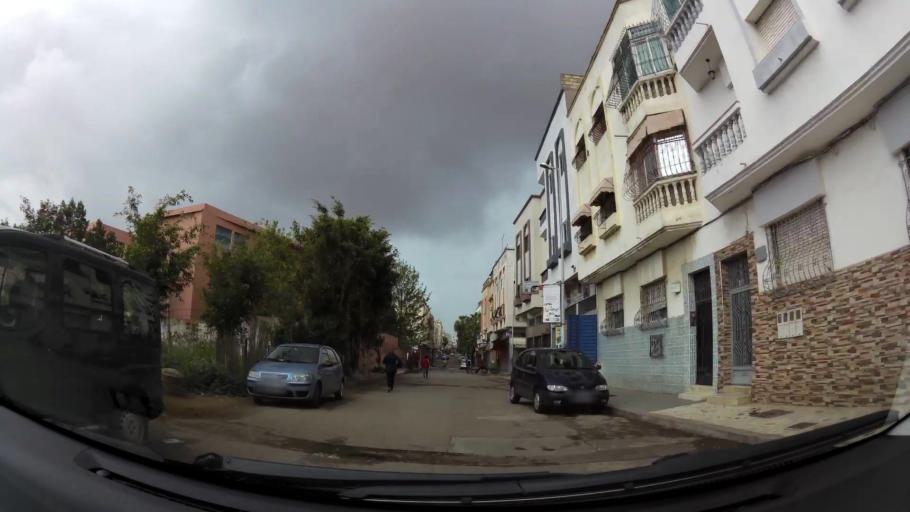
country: MA
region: Grand Casablanca
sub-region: Casablanca
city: Casablanca
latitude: 33.5417
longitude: -7.6806
